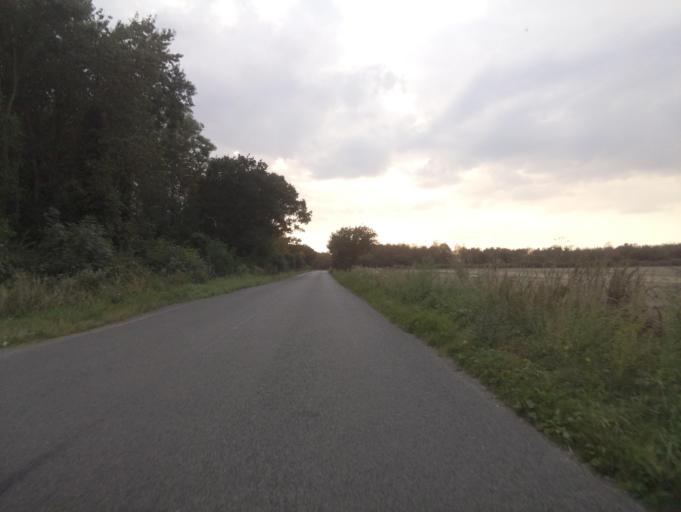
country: GB
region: England
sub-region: Nottinghamshire
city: South Collingham
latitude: 53.1429
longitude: -0.6655
